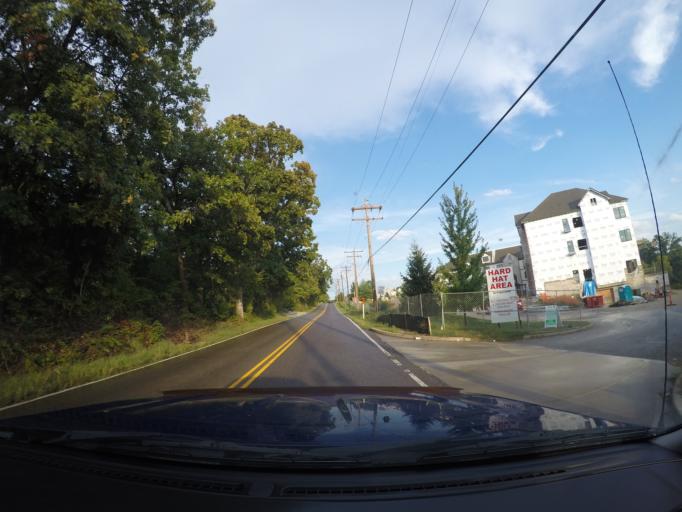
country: US
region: Missouri
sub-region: Saint Louis County
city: Sunset Hills
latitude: 38.5520
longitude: -90.4116
